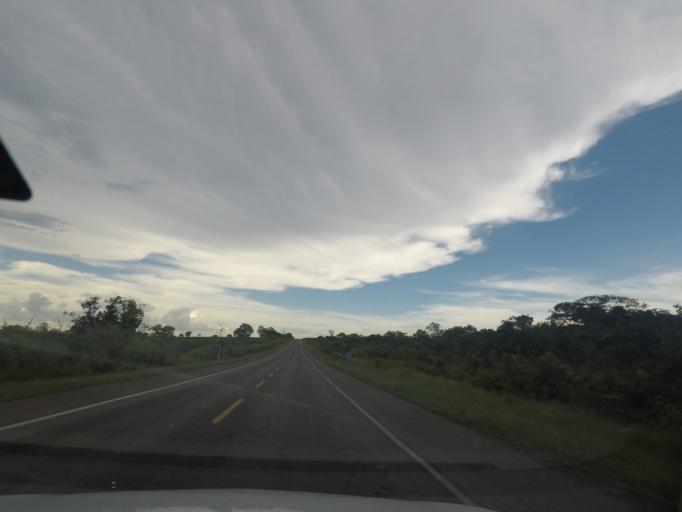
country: BR
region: Minas Gerais
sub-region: Prata
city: Prata
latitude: -19.5900
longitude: -48.8296
